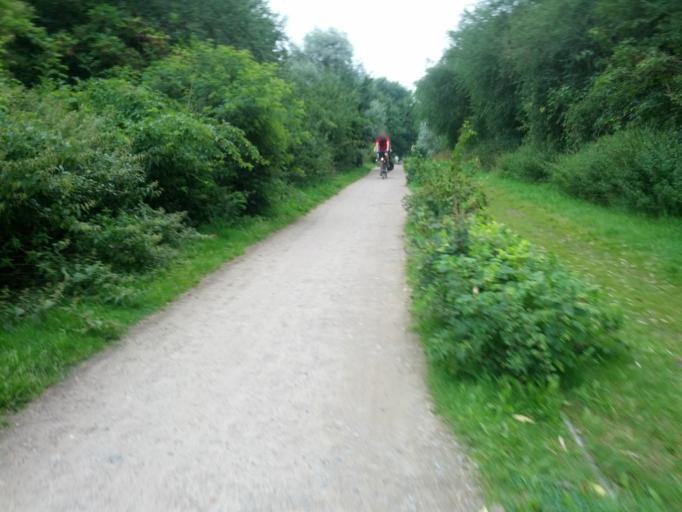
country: DE
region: Mecklenburg-Vorpommern
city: Ostseebad Kuhlungsborn
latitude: 54.1472
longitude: 11.7893
